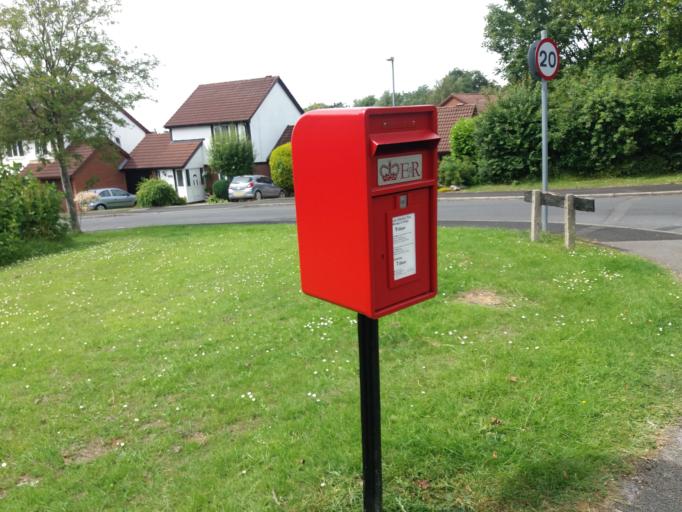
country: GB
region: England
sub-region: Lancashire
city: Clayton-le-Woods
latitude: 53.6979
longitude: -2.6445
